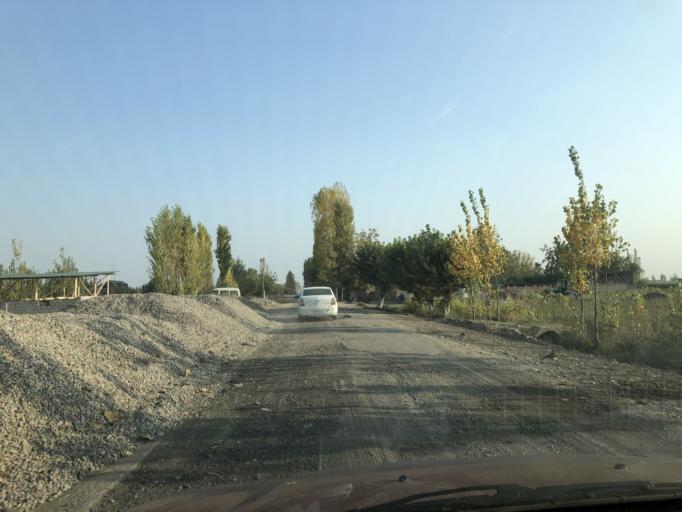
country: UZ
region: Namangan
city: Uychi
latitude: 41.0662
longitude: 71.9857
